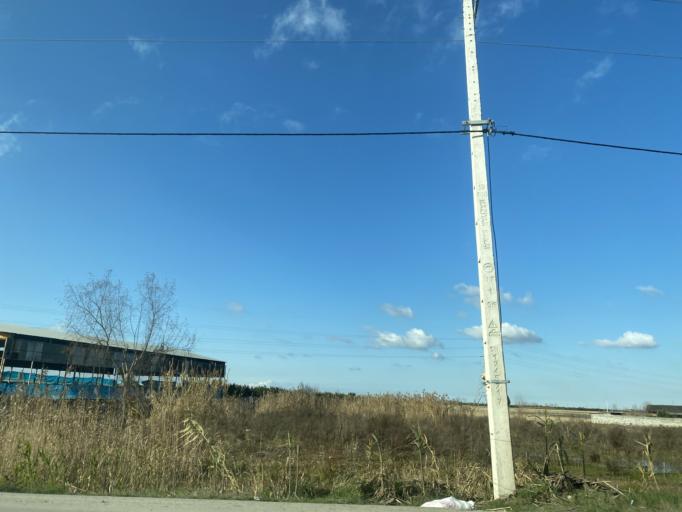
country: IR
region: Mazandaran
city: Babol
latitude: 36.5254
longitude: 52.6146
